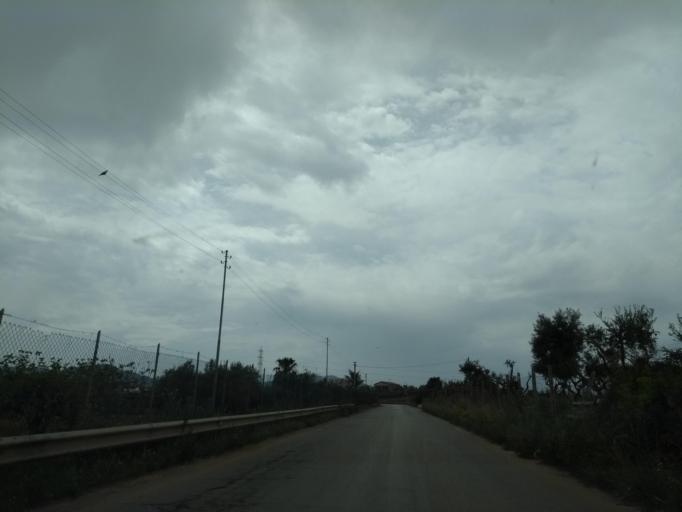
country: IT
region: Sicily
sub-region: Palermo
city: Partinico
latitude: 38.0000
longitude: 13.0664
